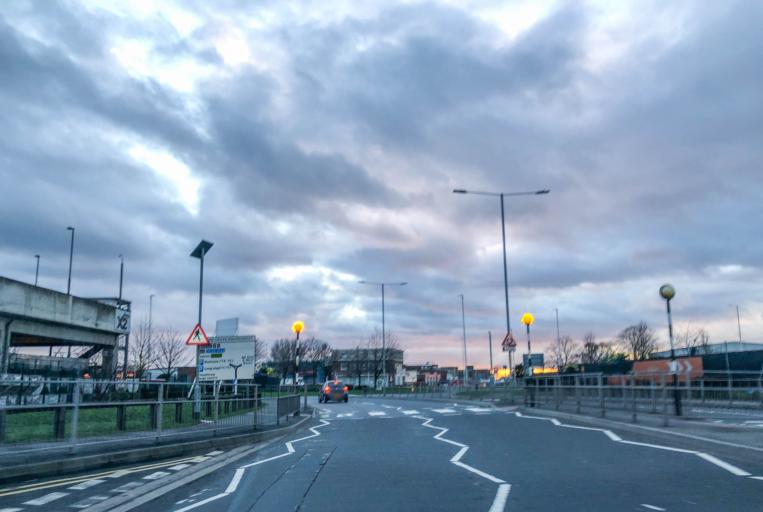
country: GB
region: England
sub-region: Greater London
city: Feltham
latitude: 51.4686
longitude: -0.4217
